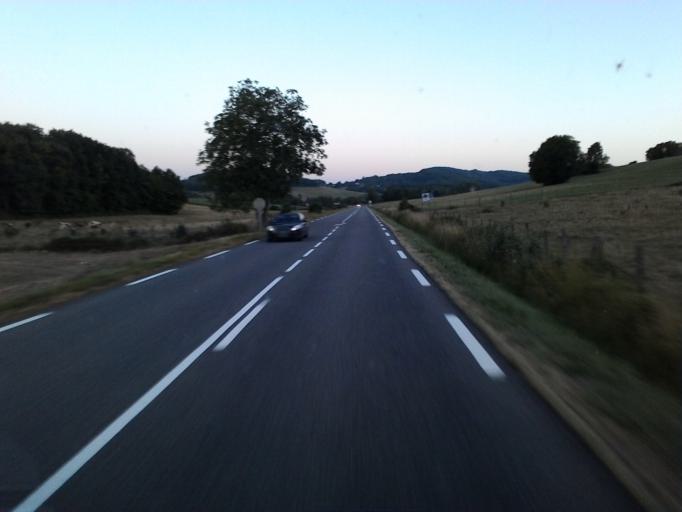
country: FR
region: Franche-Comte
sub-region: Departement du Jura
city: Poligny
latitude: 46.8224
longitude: 5.5945
